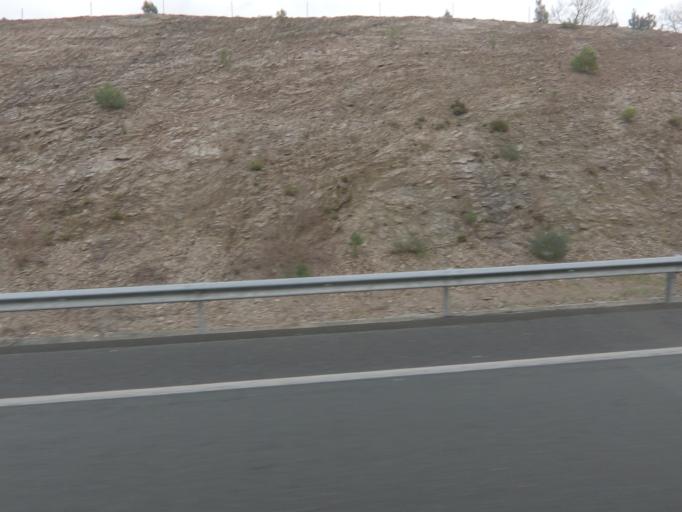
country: ES
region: Galicia
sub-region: Provincia de Pontevedra
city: Lalin
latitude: 42.6081
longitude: -8.1008
